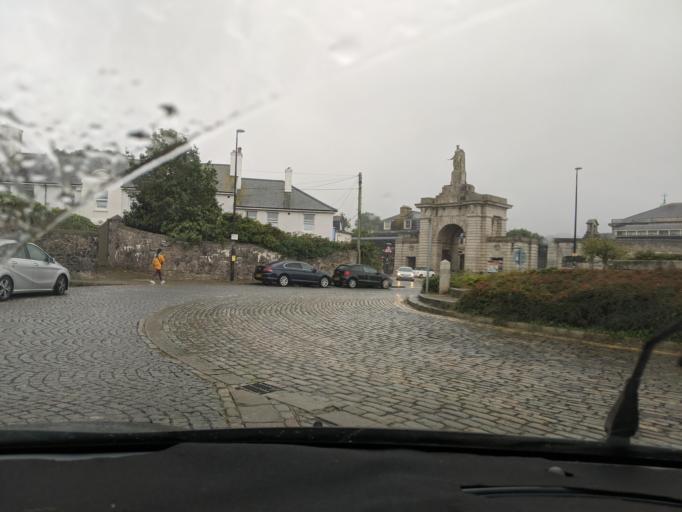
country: GB
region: England
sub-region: Plymouth
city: Plymouth
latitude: 50.3631
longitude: -4.1624
